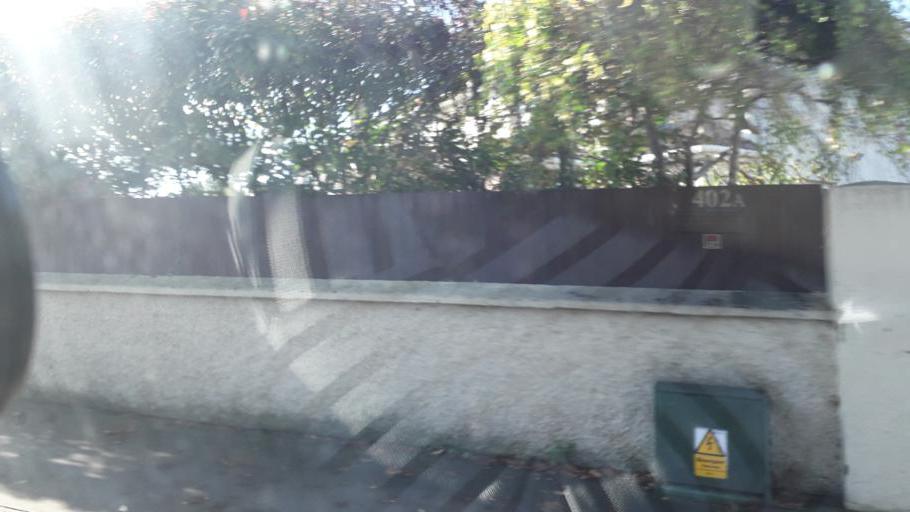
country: IE
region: Leinster
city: Raheny
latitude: 53.3777
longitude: -6.1879
